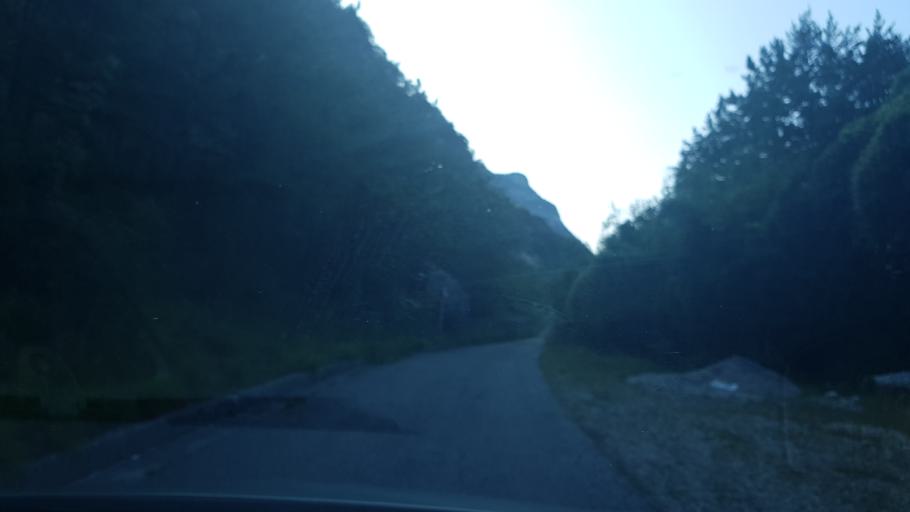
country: IT
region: Friuli Venezia Giulia
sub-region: Provincia di Udine
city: Moggio Udinese
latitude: 46.4382
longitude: 13.2077
